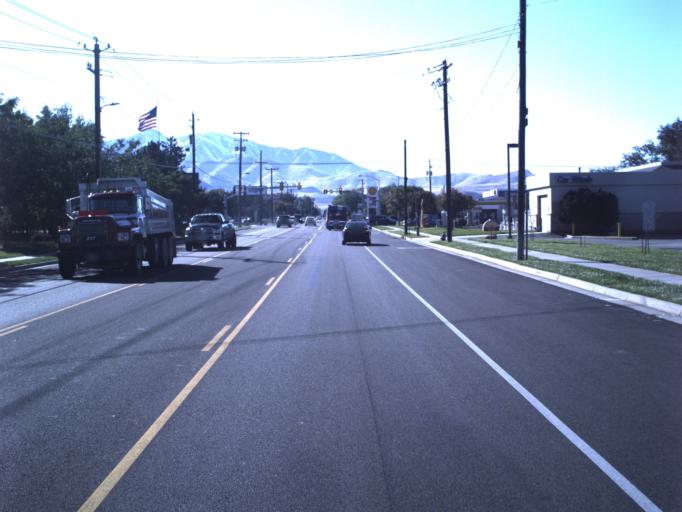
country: US
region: Utah
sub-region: Salt Lake County
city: Magna
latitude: 40.6965
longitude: -112.0612
